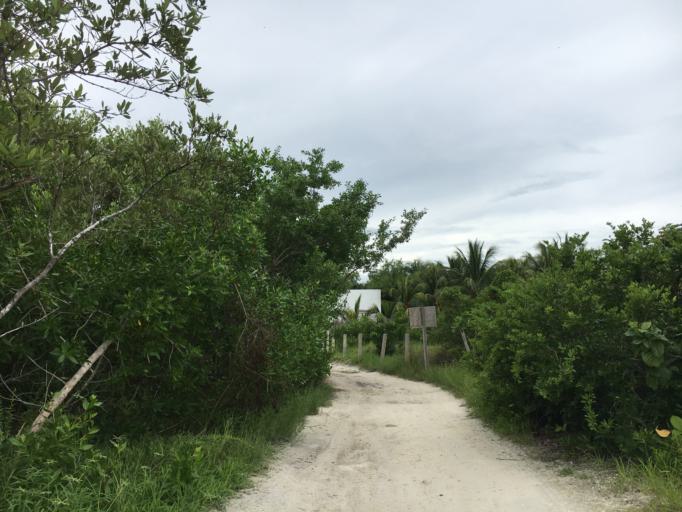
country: MX
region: Quintana Roo
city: Kantunilkin
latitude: 21.5350
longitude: -87.3629
